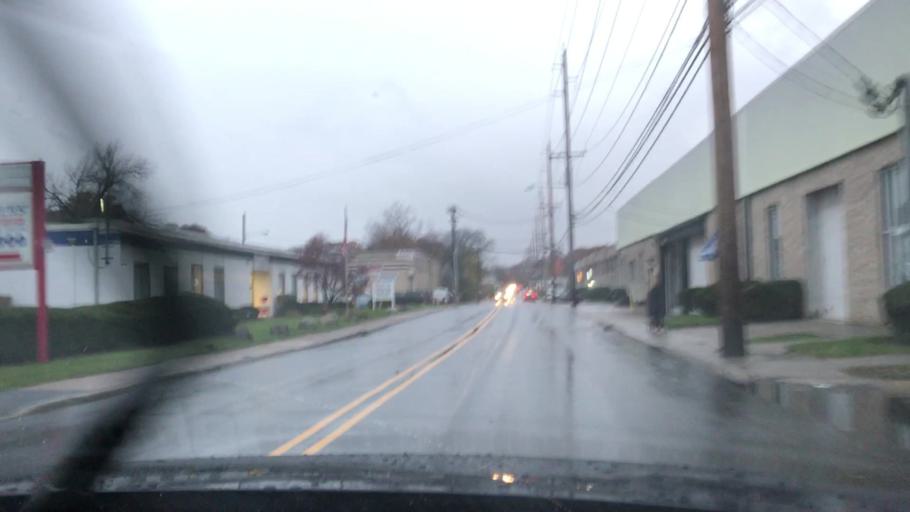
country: US
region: New Jersey
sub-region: Bergen County
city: Bergenfield
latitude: 40.9160
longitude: -74.0007
